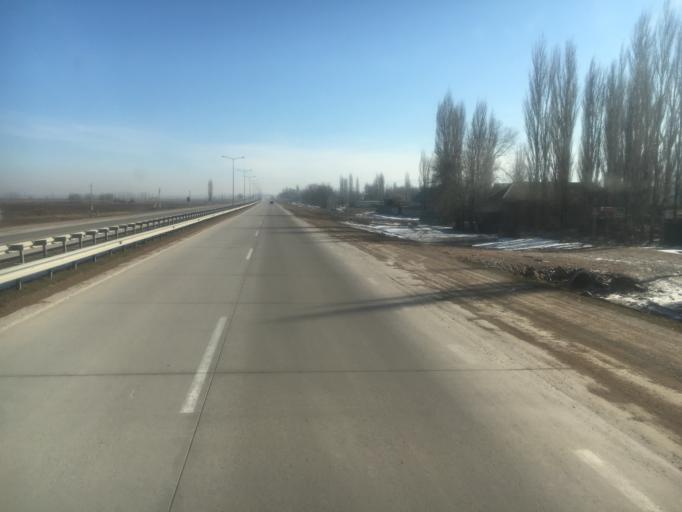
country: KZ
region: Zhambyl
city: Merke
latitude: 42.8778
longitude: 73.0984
